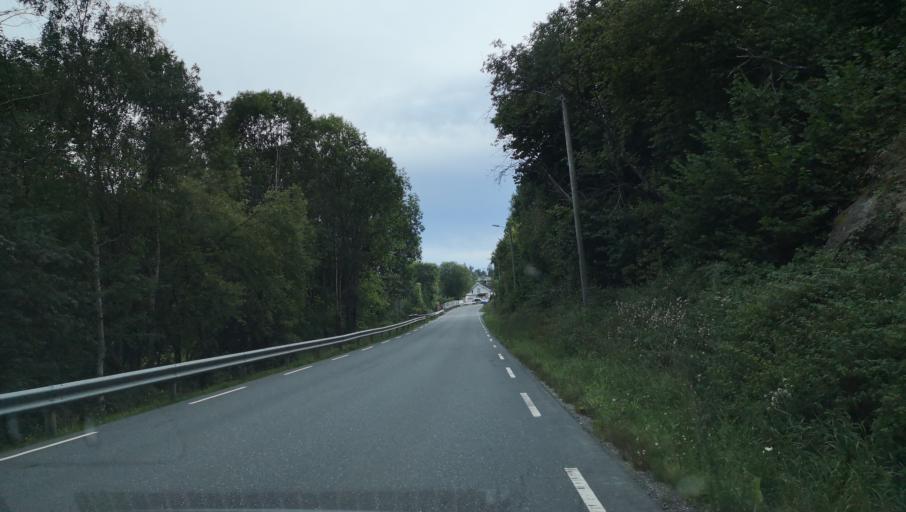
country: NO
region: Ostfold
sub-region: Hobol
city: Tomter
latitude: 59.6668
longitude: 11.0112
